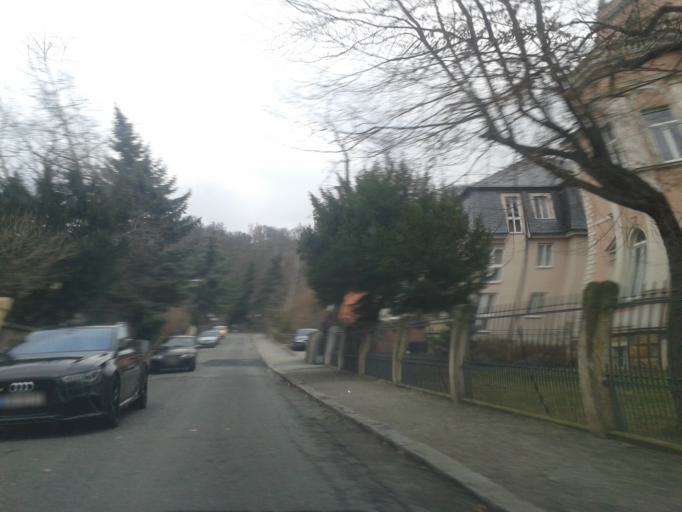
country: DE
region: Saxony
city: Radebeul
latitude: 51.1072
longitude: 13.6805
